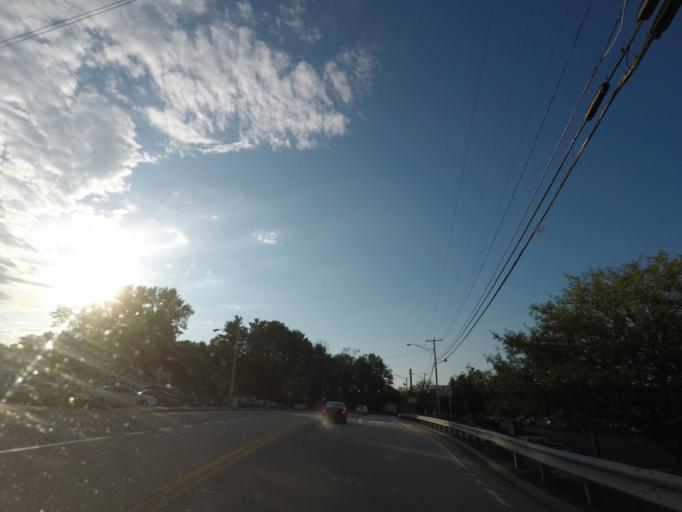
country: US
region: Massachusetts
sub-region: Worcester County
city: Sturbridge
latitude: 42.0963
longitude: -72.0718
